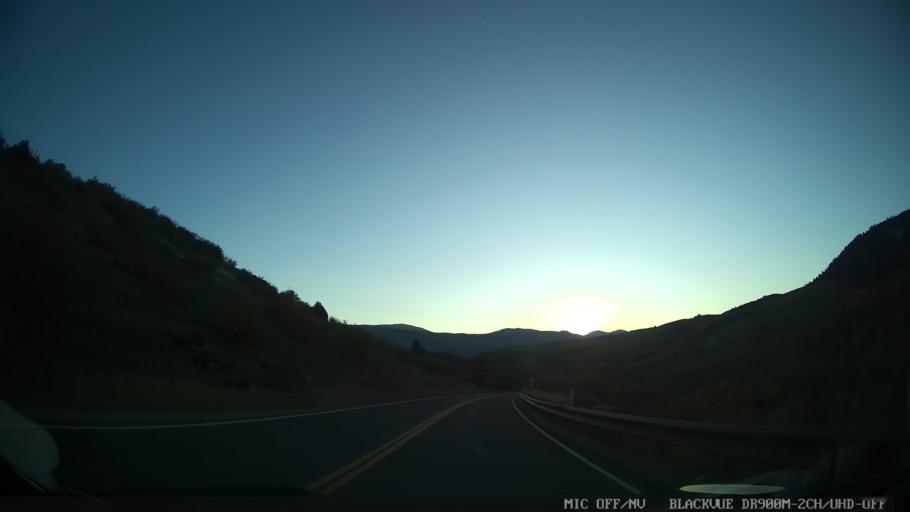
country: US
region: Colorado
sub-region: Eagle County
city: Edwards
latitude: 39.8148
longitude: -106.6665
